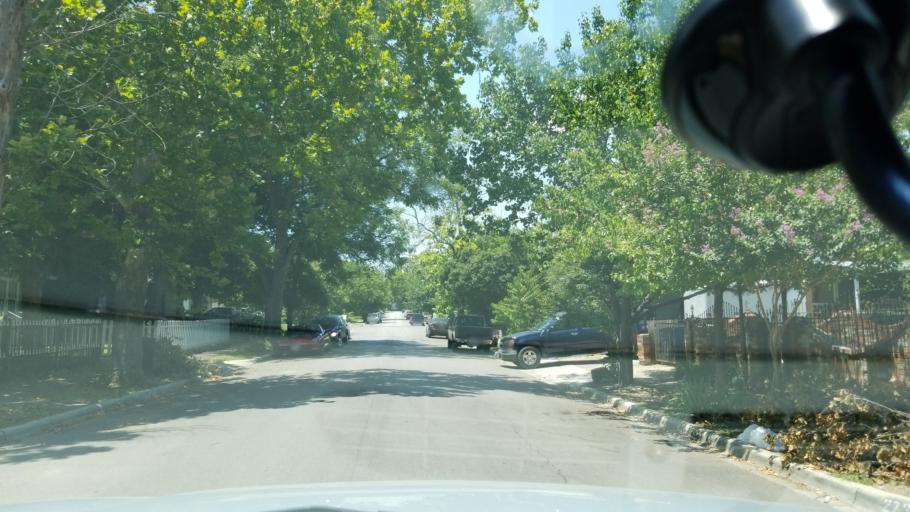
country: US
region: Texas
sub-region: Dallas County
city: Cockrell Hill
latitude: 32.7291
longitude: -96.8652
